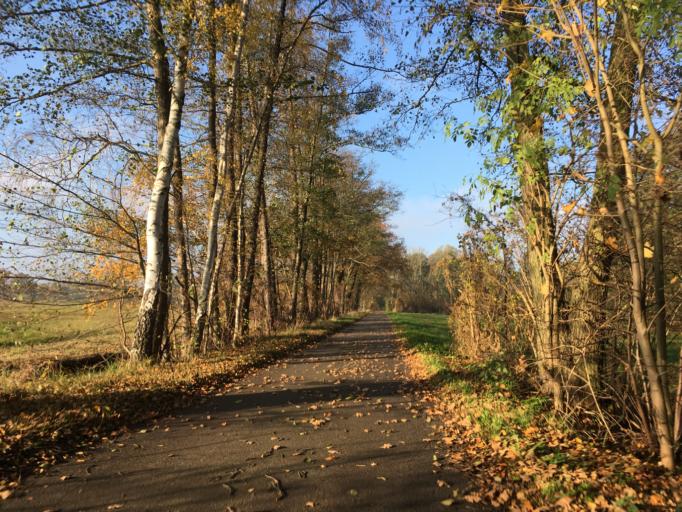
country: DE
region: Brandenburg
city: Schlepzig
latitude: 52.0438
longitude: 13.9000
